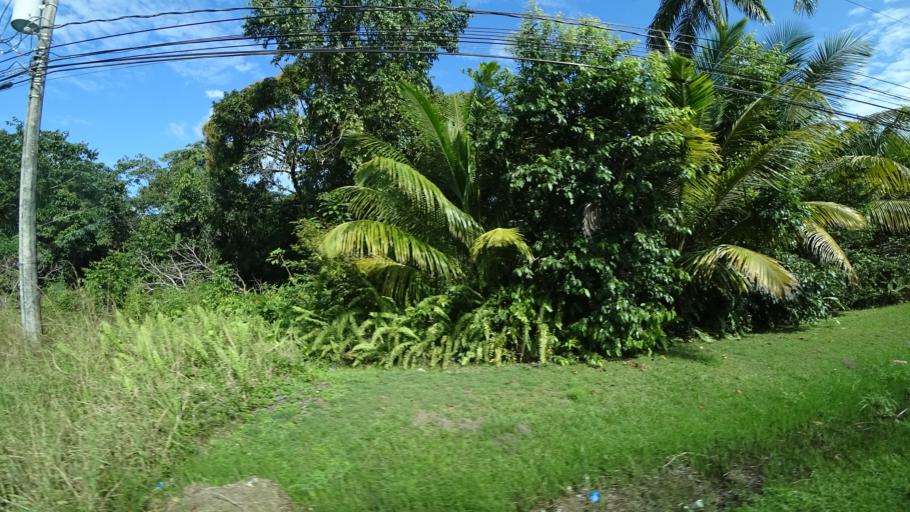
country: BZ
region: Belize
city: Belize City
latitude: 17.5692
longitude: -88.4052
